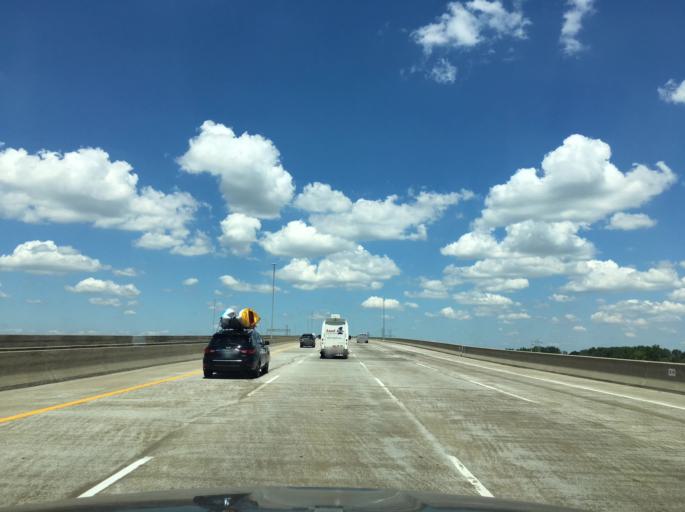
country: US
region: Michigan
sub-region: Saginaw County
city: Zilwaukee
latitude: 43.4764
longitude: -83.9036
